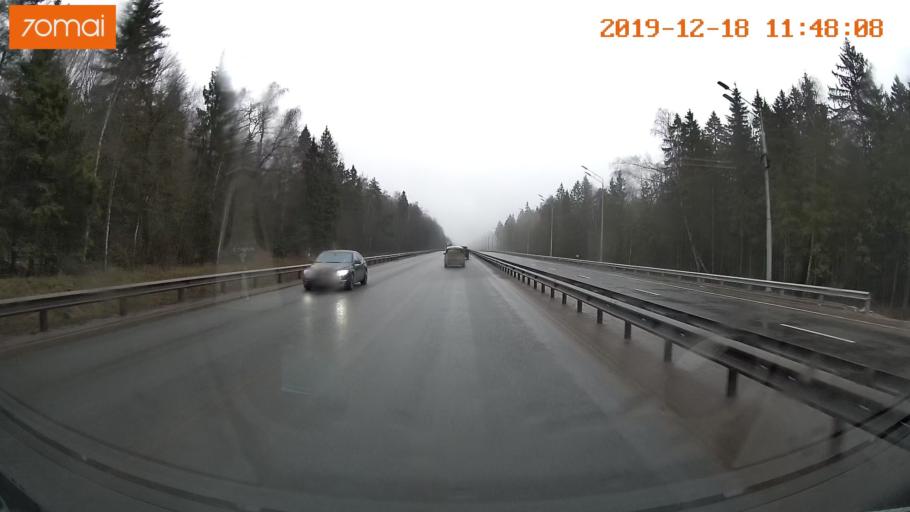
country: RU
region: Moskovskaya
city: Yershovo
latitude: 55.7650
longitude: 36.9008
